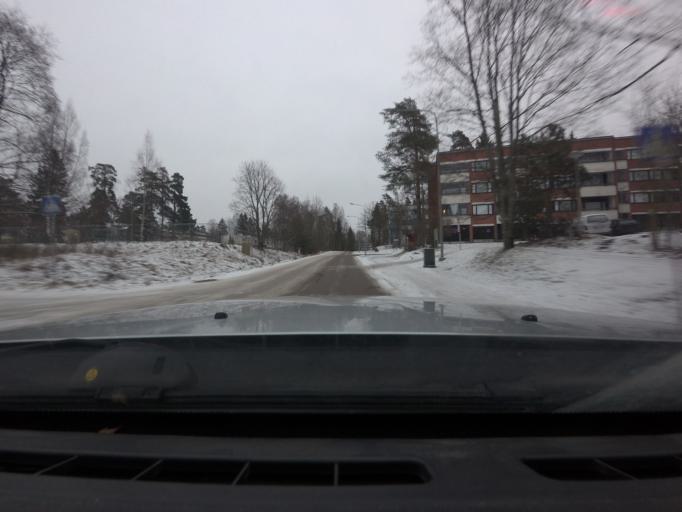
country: FI
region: Uusimaa
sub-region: Helsinki
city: Kauniainen
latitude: 60.2287
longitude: 24.7423
